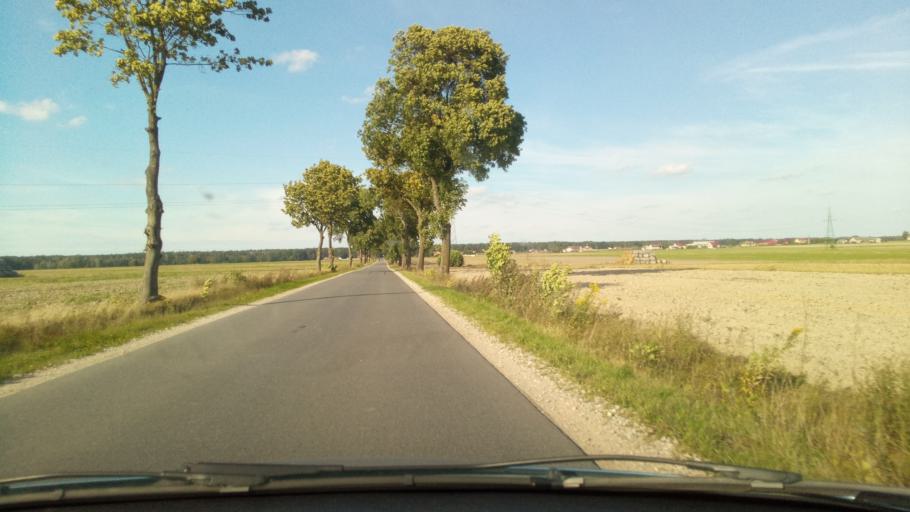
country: PL
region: Lodz Voivodeship
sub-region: Powiat piotrkowski
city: Sulejow
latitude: 51.3942
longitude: 19.8217
